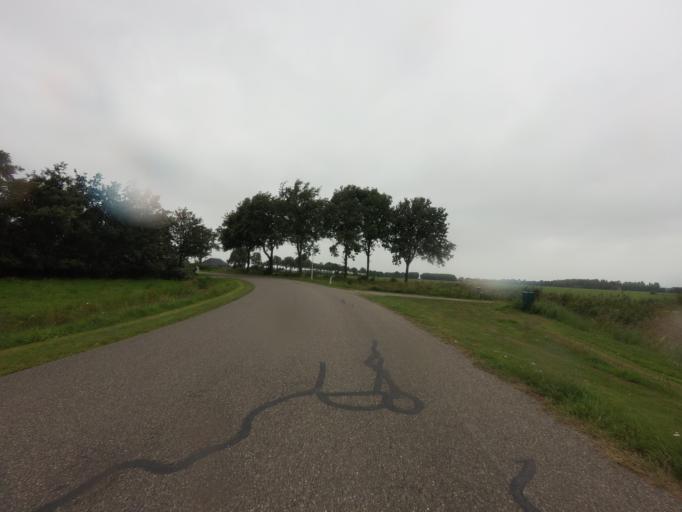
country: NL
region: Friesland
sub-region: Gemeente Opsterland
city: Tijnje
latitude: 53.0280
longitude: 5.9792
